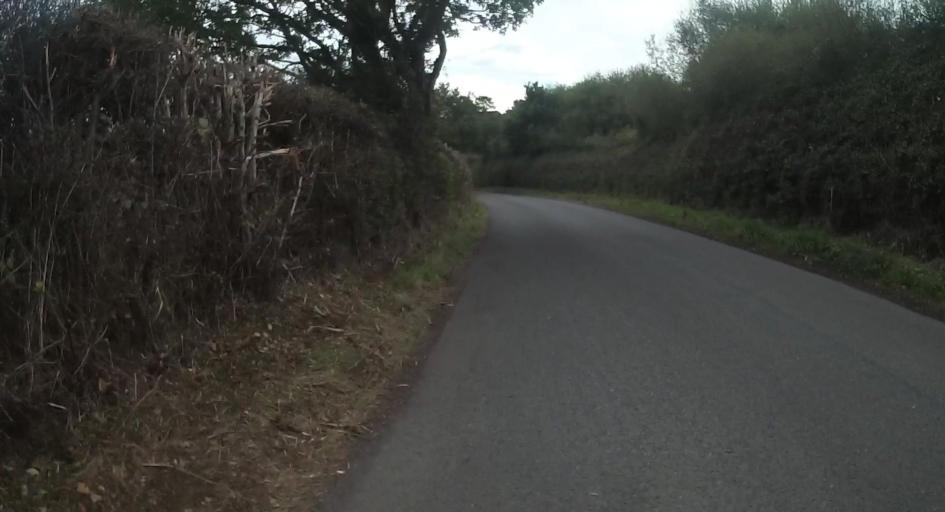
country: GB
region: England
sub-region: Hampshire
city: Fleet
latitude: 51.2880
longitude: -0.8901
